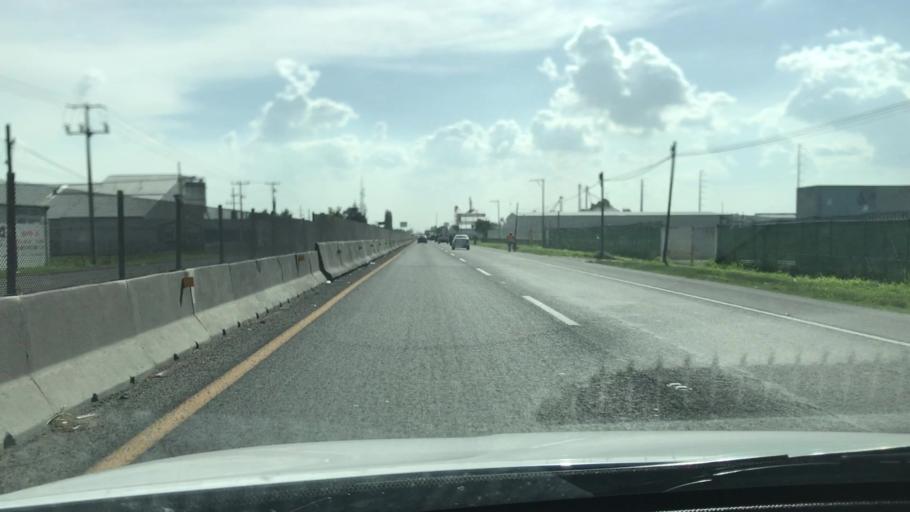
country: MX
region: Guanajuato
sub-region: Cortazar
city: Colonia la Calzada (La Olla)
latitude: 20.5120
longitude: -100.9432
